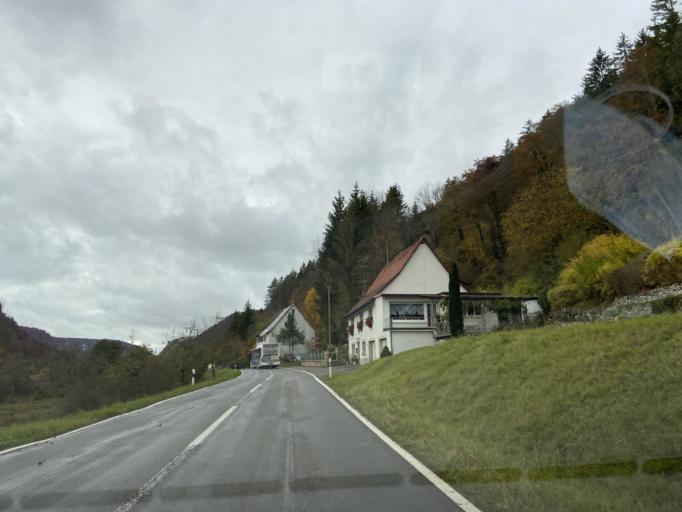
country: DE
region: Baden-Wuerttemberg
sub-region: Tuebingen Region
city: Stetten am Kalten Markt
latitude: 48.0932
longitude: 9.0545
